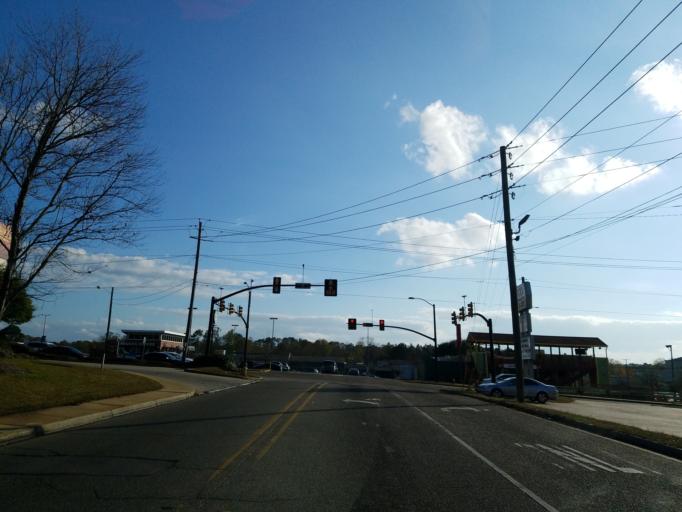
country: US
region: Mississippi
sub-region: Lamar County
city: Arnold Line
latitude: 31.3254
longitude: -89.3455
